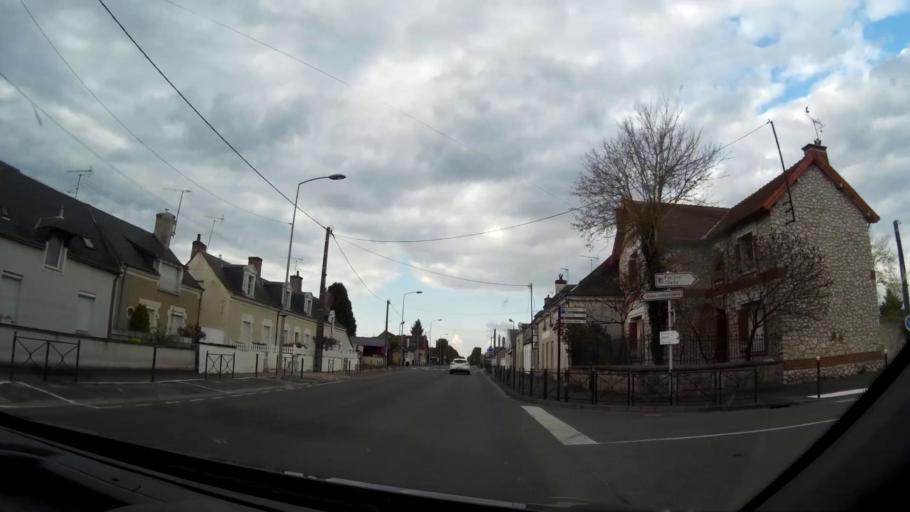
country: FR
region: Centre
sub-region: Departement du Loir-et-Cher
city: Contres
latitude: 47.4210
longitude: 1.4287
